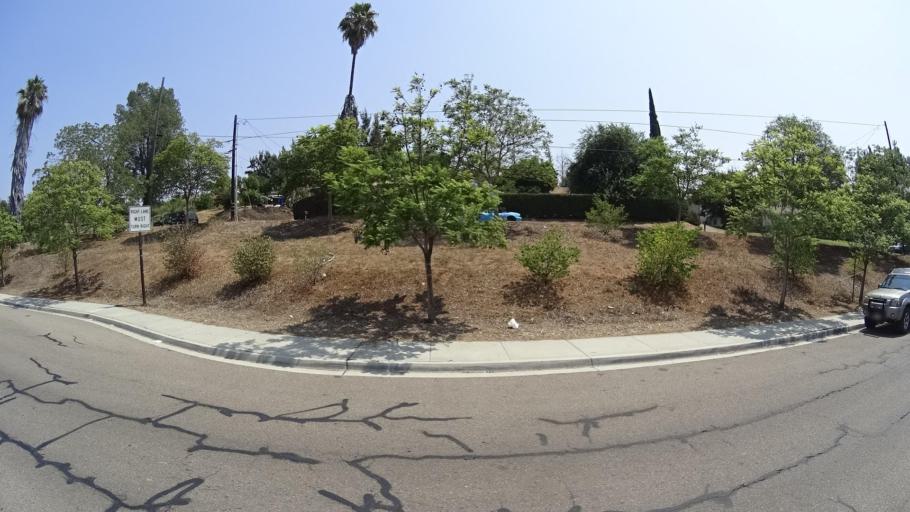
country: US
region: California
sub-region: San Diego County
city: Fallbrook
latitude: 33.3649
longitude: -117.2496
